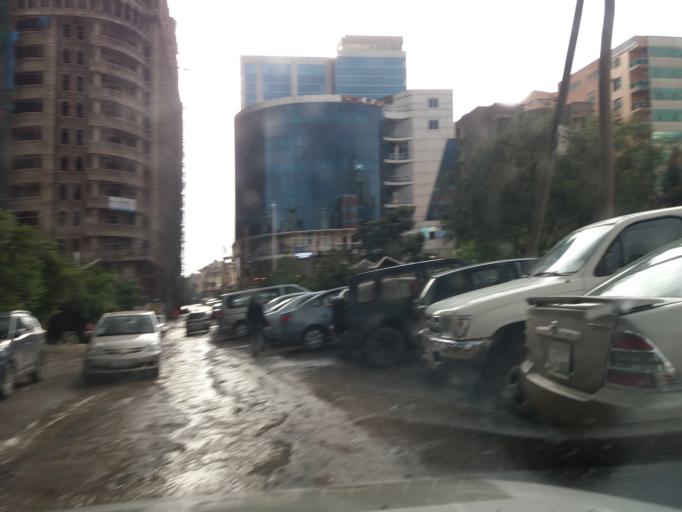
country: ET
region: Adis Abeba
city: Addis Ababa
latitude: 8.9951
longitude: 38.7859
